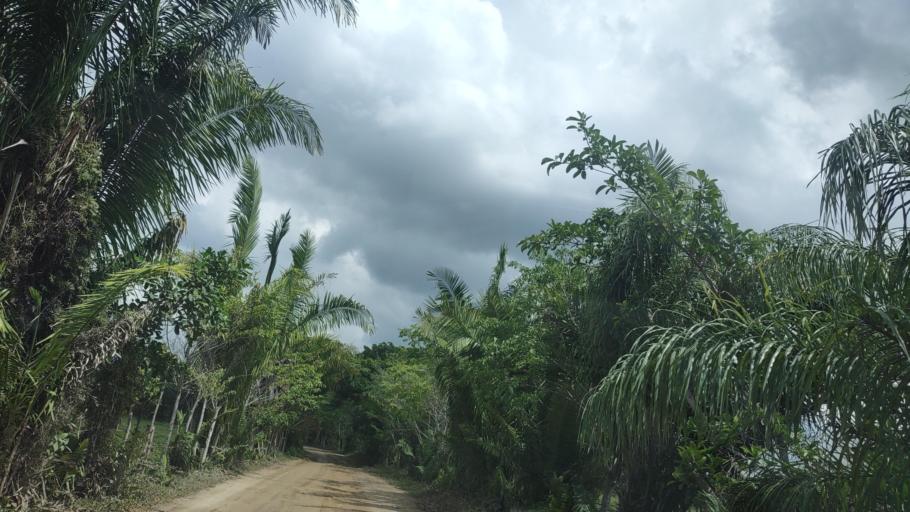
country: MX
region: Veracruz
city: Las Choapas
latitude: 17.9632
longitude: -94.1236
